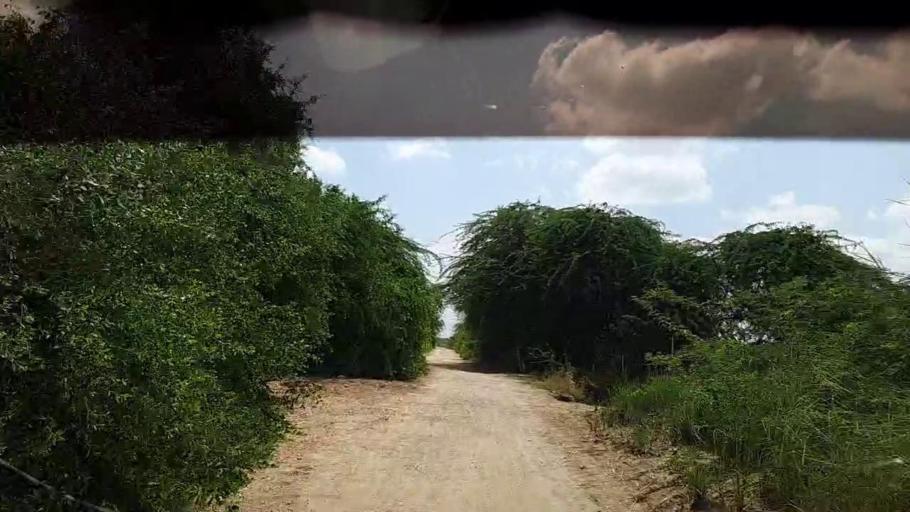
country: PK
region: Sindh
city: Kadhan
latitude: 24.5879
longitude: 68.9584
